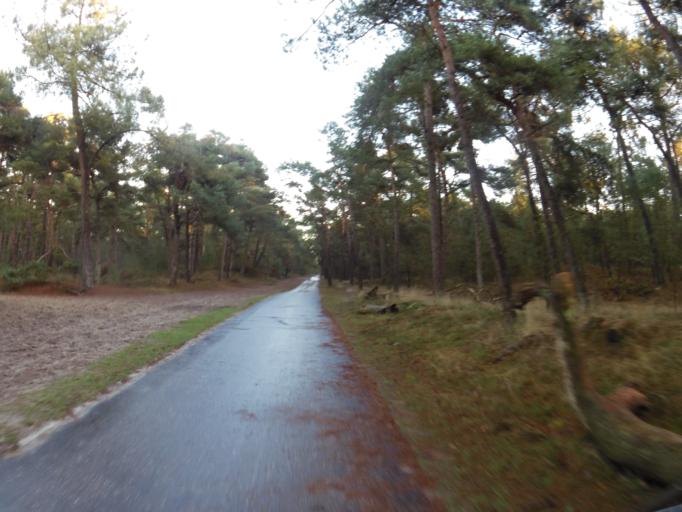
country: NL
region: North Brabant
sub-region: Gemeente Loon op Zand
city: Loon op Zand
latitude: 51.6382
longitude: 5.1011
